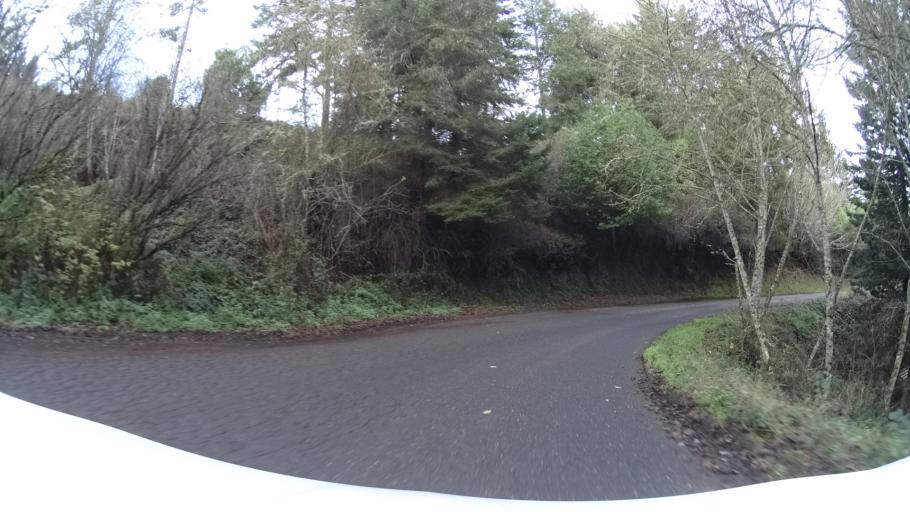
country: US
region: California
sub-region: Humboldt County
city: Ferndale
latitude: 40.5751
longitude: -124.2674
